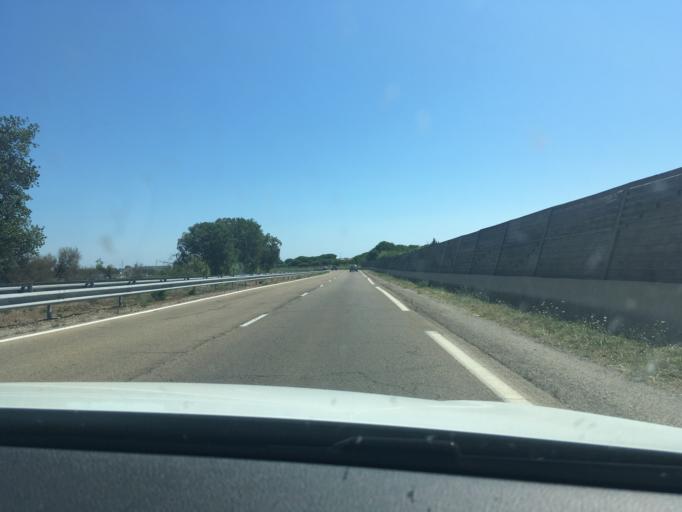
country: FR
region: Languedoc-Roussillon
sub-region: Departement du Gard
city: Le Grau-du-Roi
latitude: 43.5474
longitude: 4.1340
